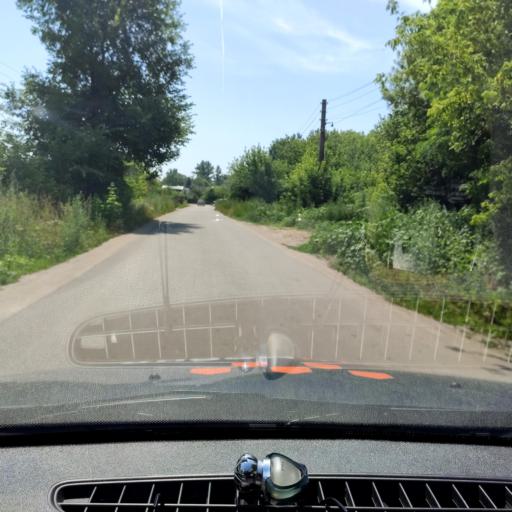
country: RU
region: Voronezj
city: Ramon'
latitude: 51.8296
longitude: 39.2664
